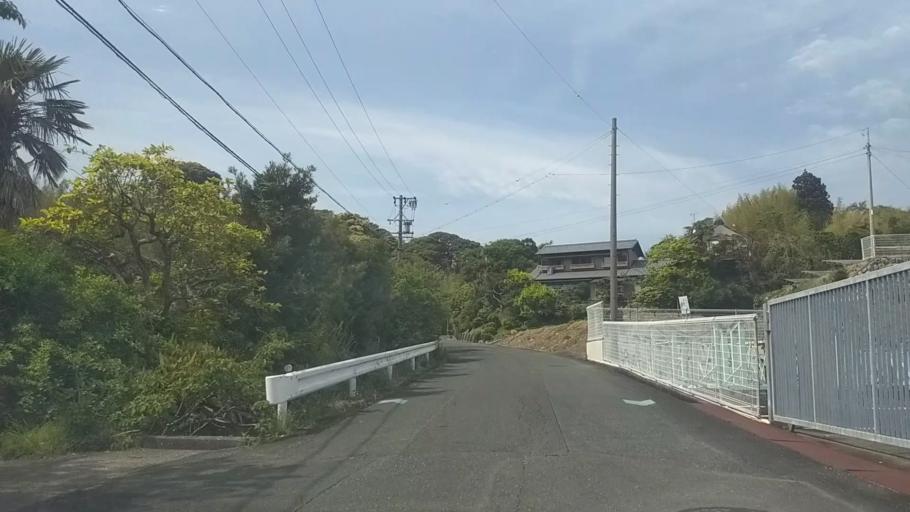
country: JP
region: Shizuoka
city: Kosai-shi
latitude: 34.7695
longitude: 137.6281
